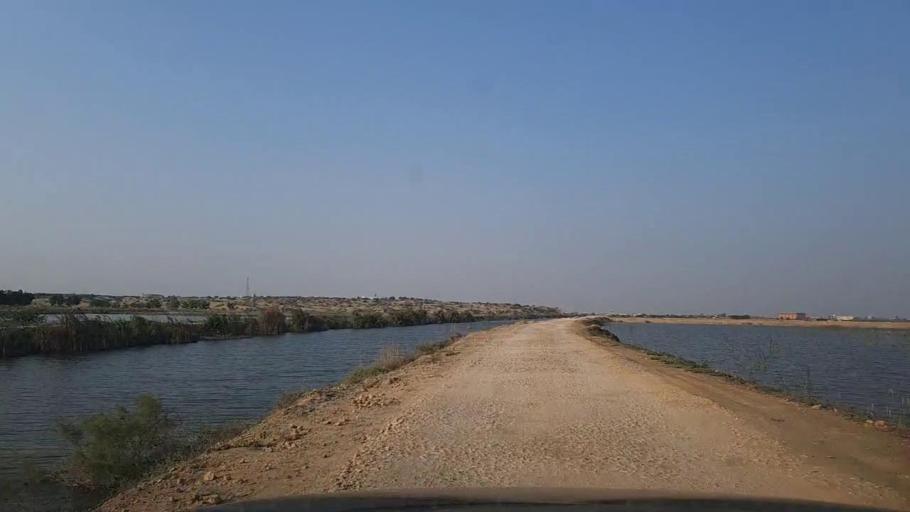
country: PK
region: Sindh
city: Thatta
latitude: 24.7358
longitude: 67.9064
